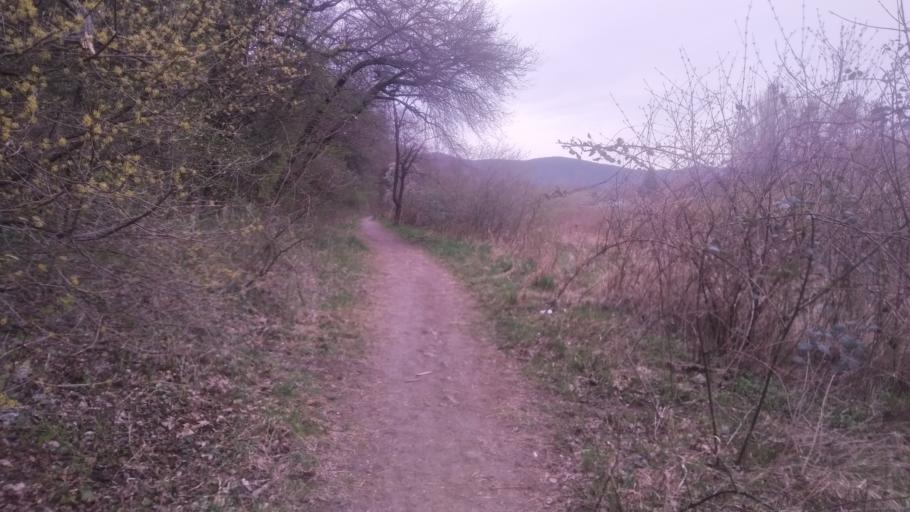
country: HU
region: Pest
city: Szentendre
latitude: 47.6820
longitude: 19.0447
